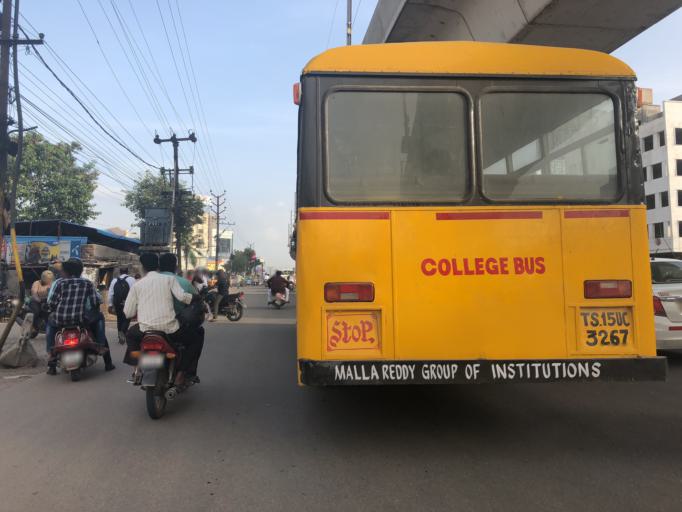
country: IN
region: Telangana
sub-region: Rangareddi
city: Kukatpalli
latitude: 17.4692
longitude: 78.4281
